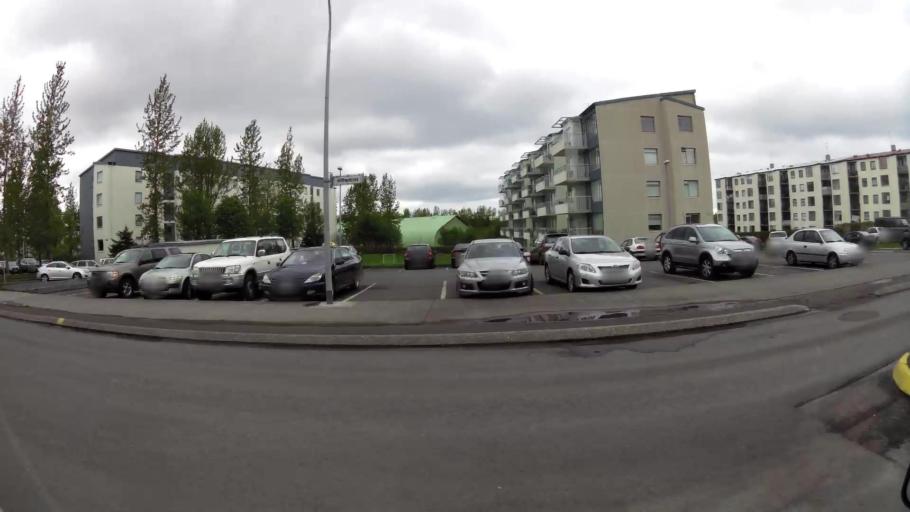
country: IS
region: Capital Region
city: Reykjavik
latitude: 64.1350
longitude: -21.8635
